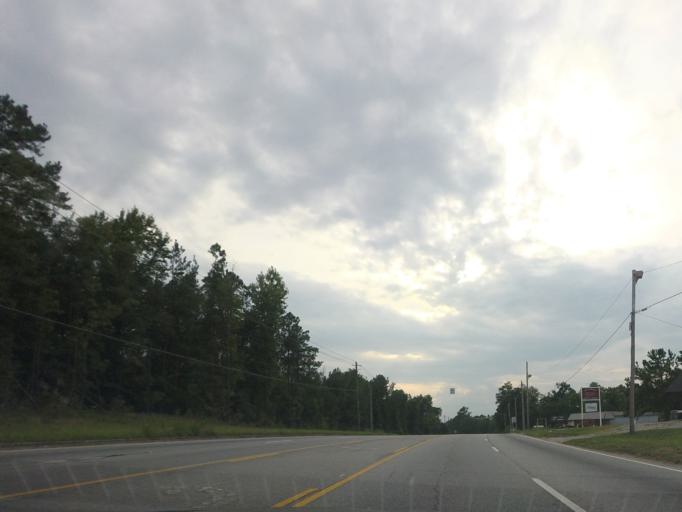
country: US
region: Georgia
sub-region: Bibb County
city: Macon
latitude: 32.8420
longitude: -83.5637
